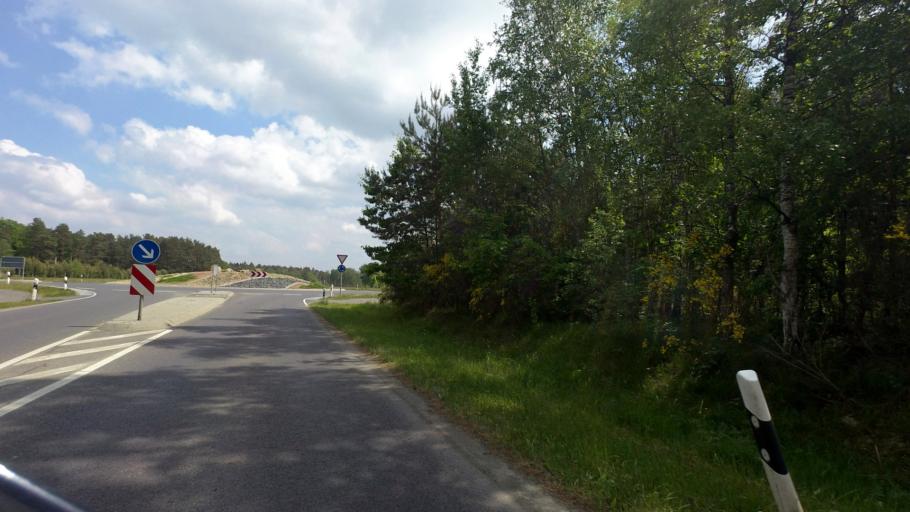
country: DE
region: Saxony
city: Krauschwitz
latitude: 51.5023
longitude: 14.7112
